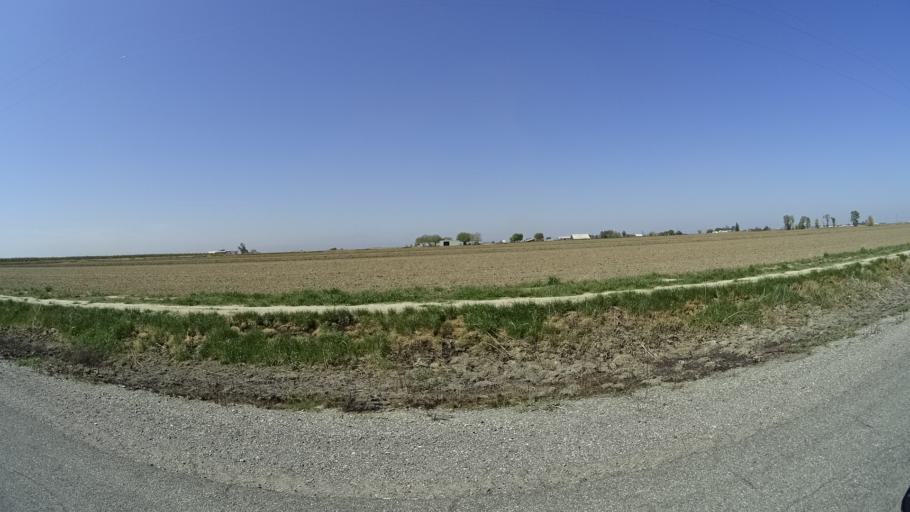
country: US
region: California
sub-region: Glenn County
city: Willows
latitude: 39.5179
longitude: -122.1029
